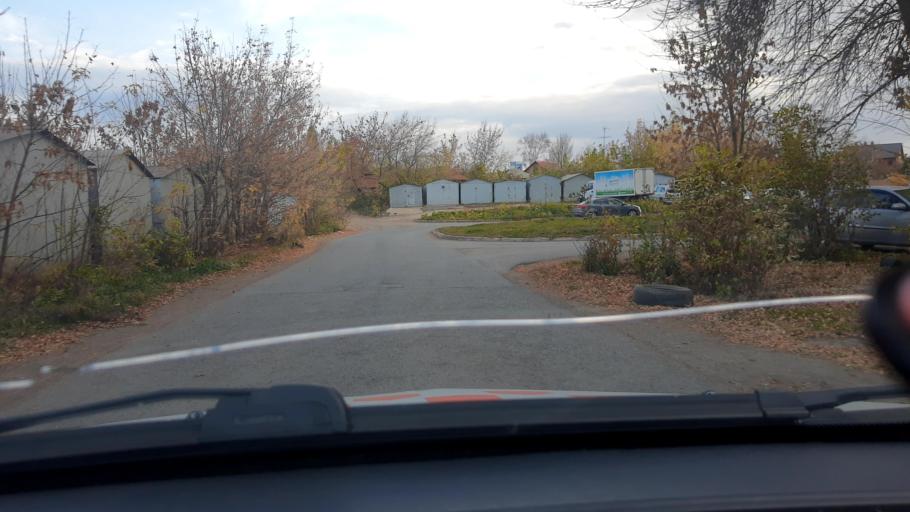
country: RU
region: Bashkortostan
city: Ufa
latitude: 54.8096
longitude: 56.1379
